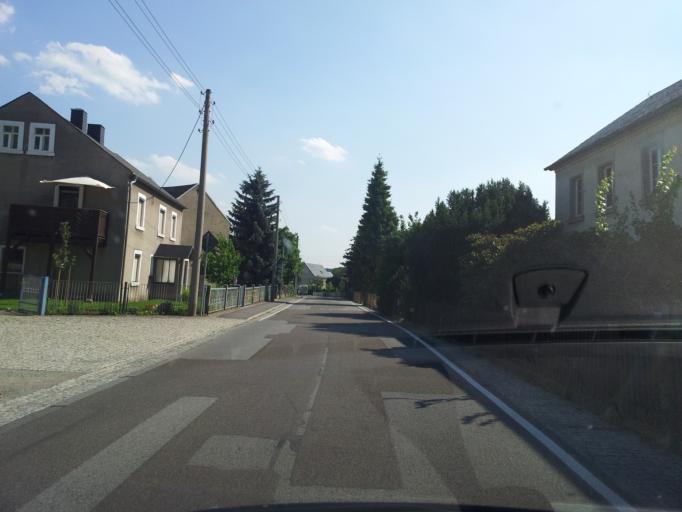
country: DE
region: Saxony
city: Wachau
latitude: 51.1945
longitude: 13.8958
